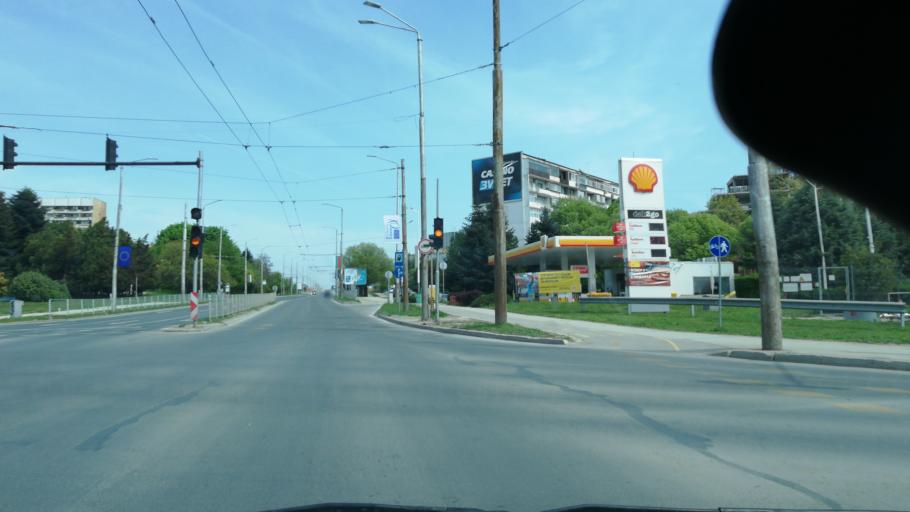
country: BG
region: Varna
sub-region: Obshtina Varna
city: Varna
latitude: 43.2279
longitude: 27.8778
